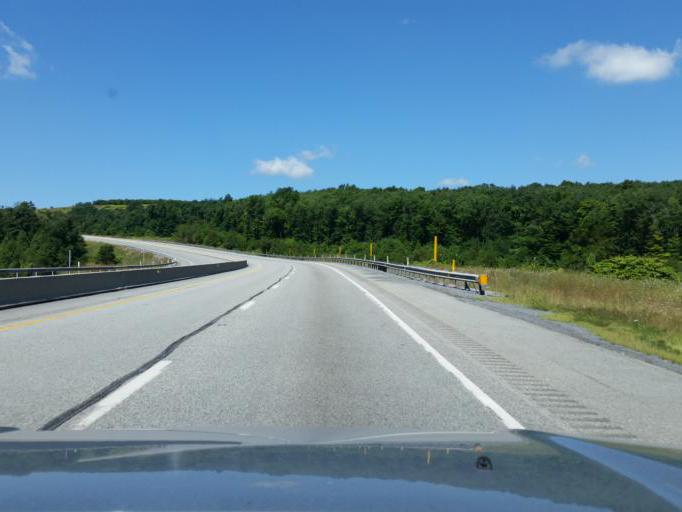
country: US
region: Pennsylvania
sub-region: Cambria County
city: Mundys Corner
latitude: 40.4516
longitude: -78.8699
